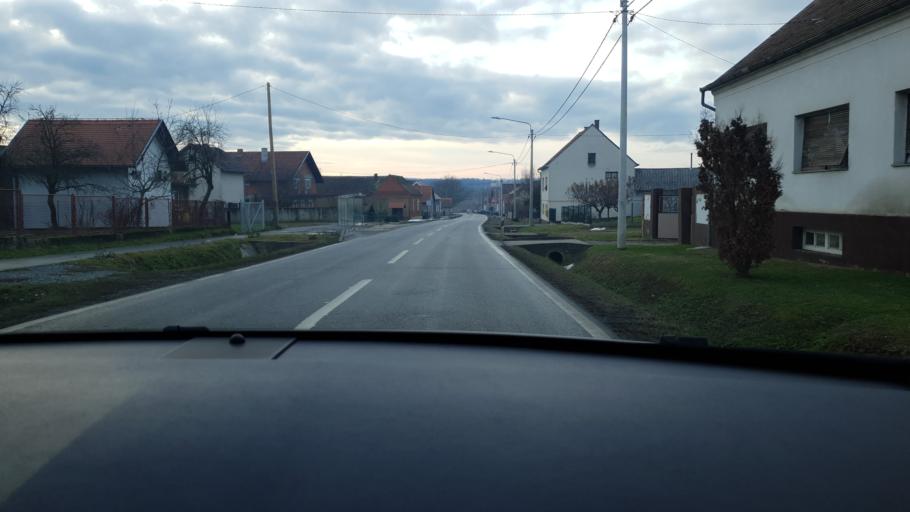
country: HR
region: Pozesko-Slavonska
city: Vidovci
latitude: 45.3572
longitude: 17.7331
